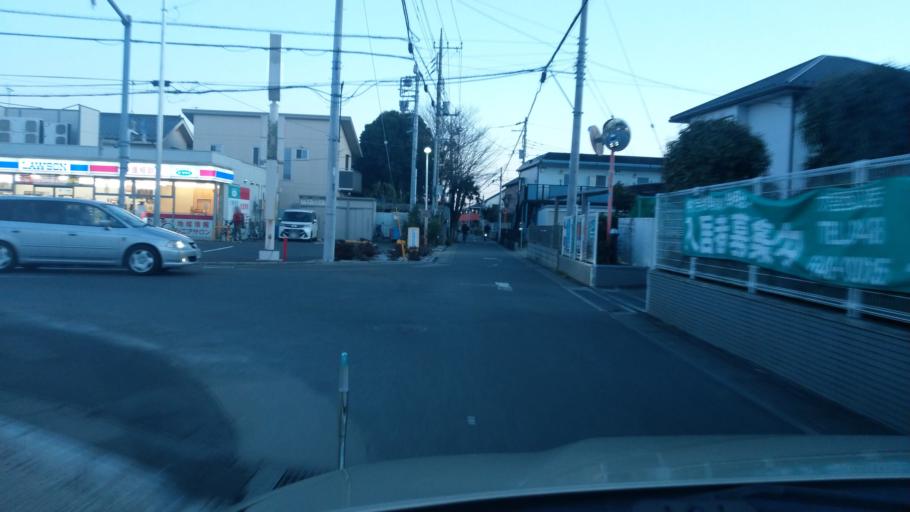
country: JP
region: Saitama
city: Yono
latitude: 35.9165
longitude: 139.5843
